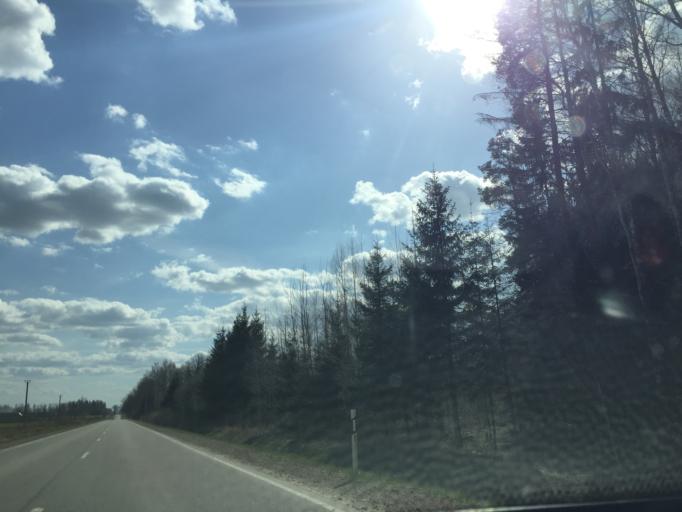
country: LV
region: Skriveri
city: Skriveri
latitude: 56.7534
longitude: 25.1696
